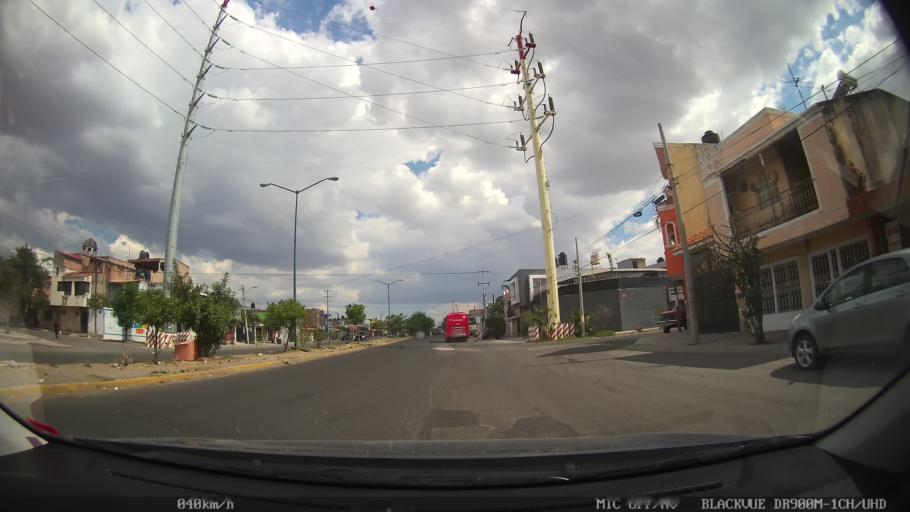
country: MX
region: Jalisco
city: Tlaquepaque
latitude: 20.6809
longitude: -103.2578
